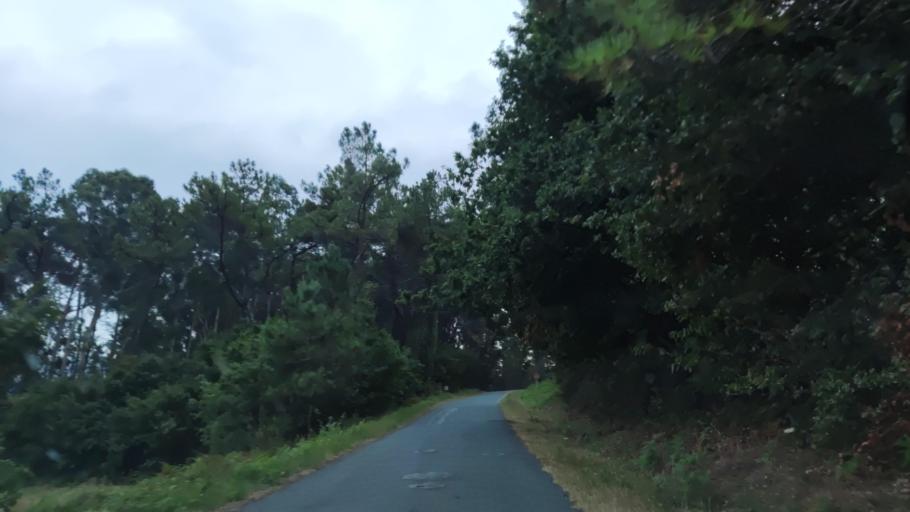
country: ES
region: Galicia
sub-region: Provincia de Pontevedra
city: Catoira
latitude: 42.6917
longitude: -8.7330
